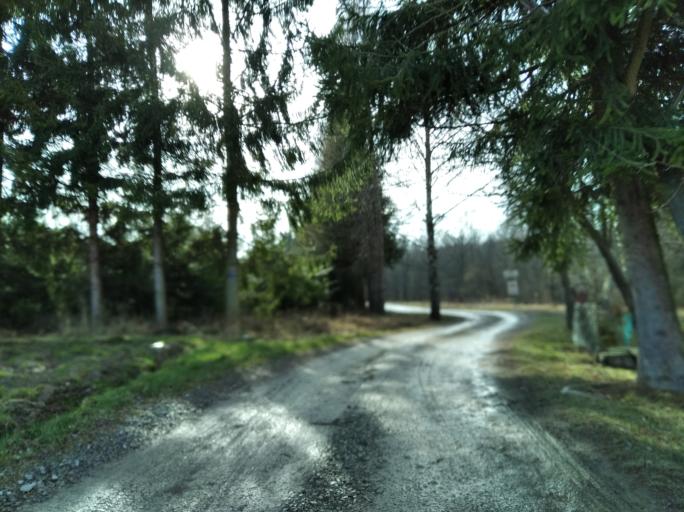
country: PL
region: Subcarpathian Voivodeship
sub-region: Powiat brzozowski
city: Grabownica Starzenska
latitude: 49.6450
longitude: 22.0660
